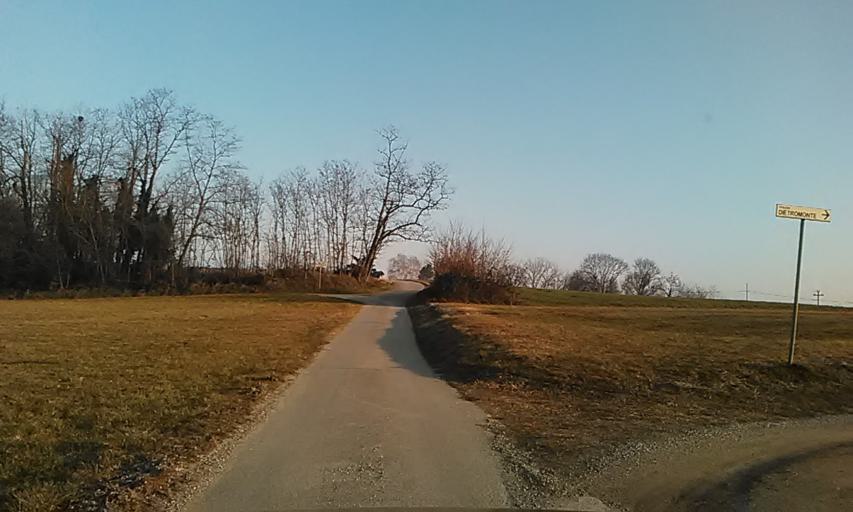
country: IT
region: Piedmont
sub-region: Provincia di Biella
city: Dorzano
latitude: 45.4152
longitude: 8.1150
